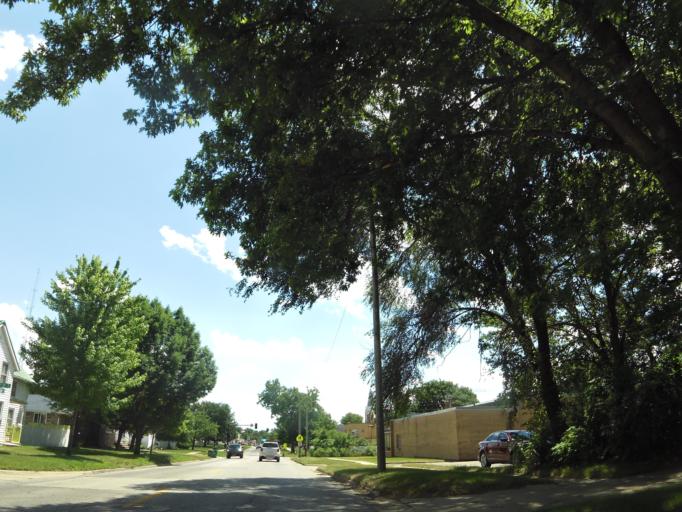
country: US
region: Iowa
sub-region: Buchanan County
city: Independence
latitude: 42.4721
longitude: -91.8895
